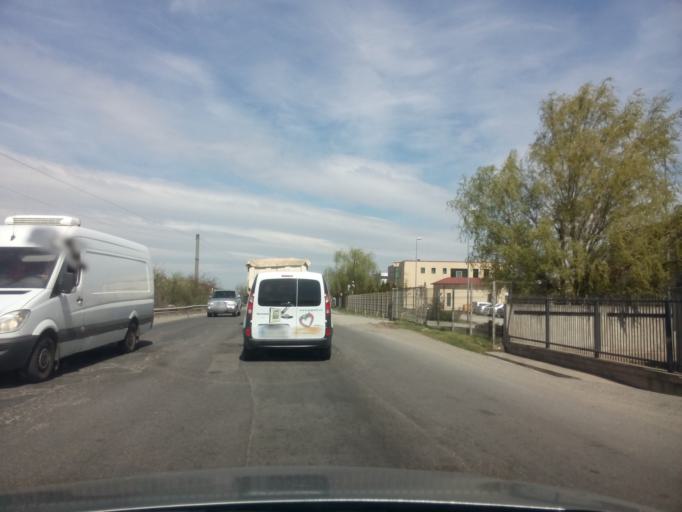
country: RO
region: Ilfov
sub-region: Comuna Pantelimon
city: Pantelimon
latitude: 44.4520
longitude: 26.2358
